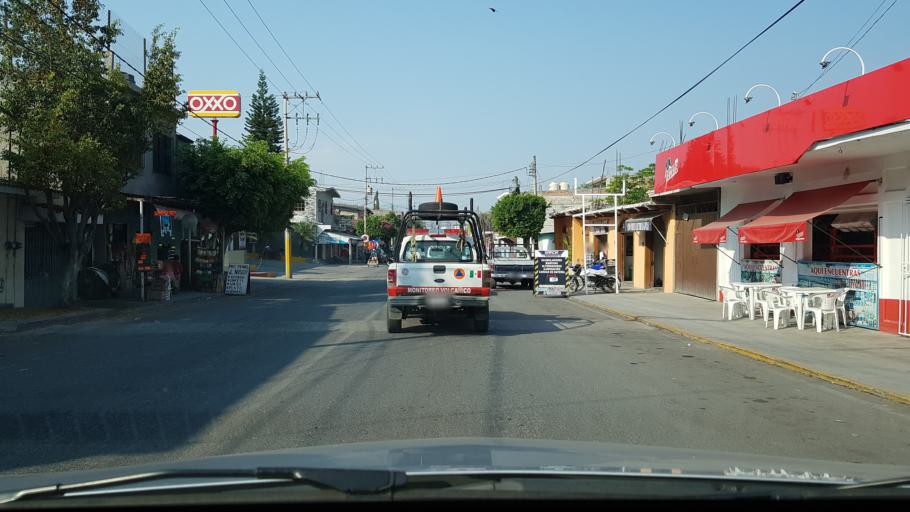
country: MX
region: Morelos
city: Tlaquiltenango
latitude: 18.6402
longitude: -99.1587
